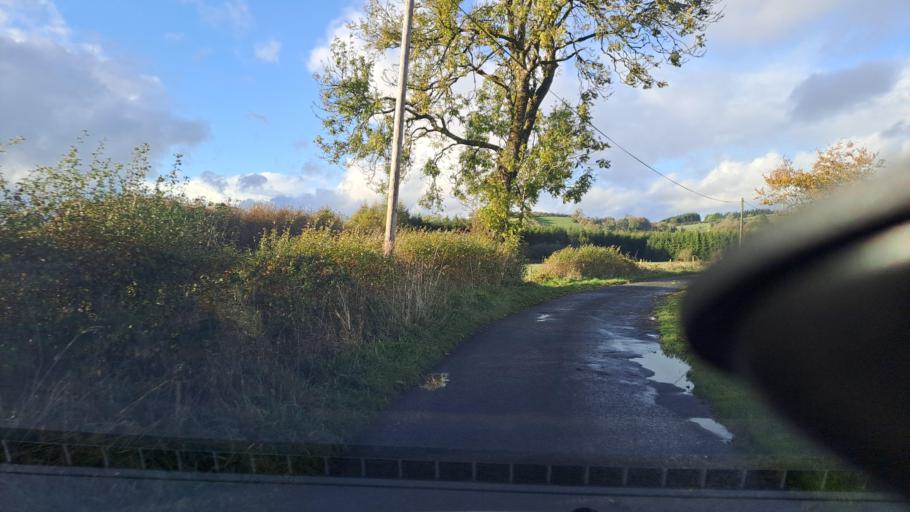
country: IE
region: Ulster
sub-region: An Cabhan
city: Bailieborough
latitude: 53.9296
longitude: -6.9411
